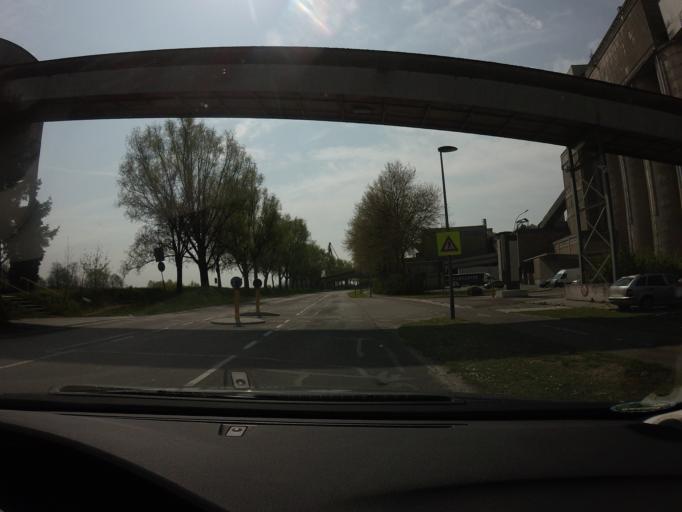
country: NL
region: Limburg
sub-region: Gemeente Maastricht
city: Maastricht
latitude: 50.8222
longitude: 5.6963
